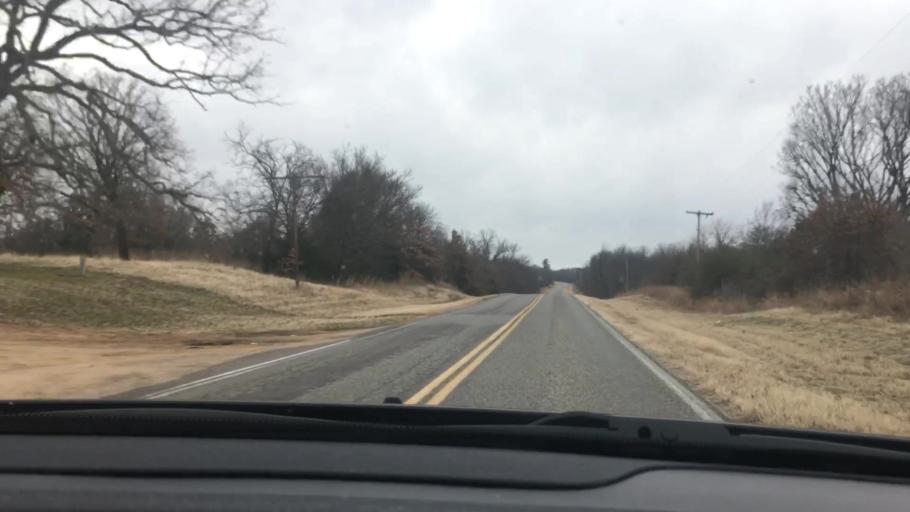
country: US
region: Oklahoma
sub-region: Johnston County
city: Tishomingo
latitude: 34.2195
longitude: -96.6362
